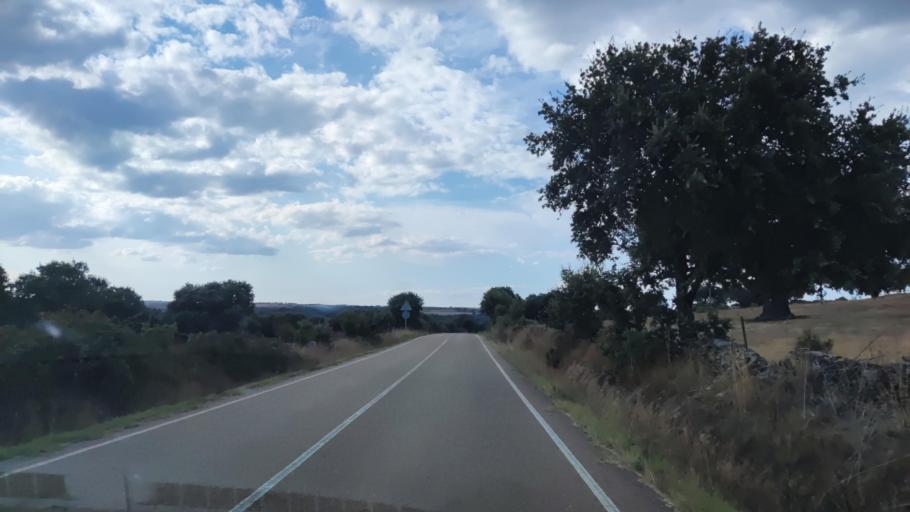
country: ES
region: Castille and Leon
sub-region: Provincia de Salamanca
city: Pastores
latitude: 40.4870
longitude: -6.4939
